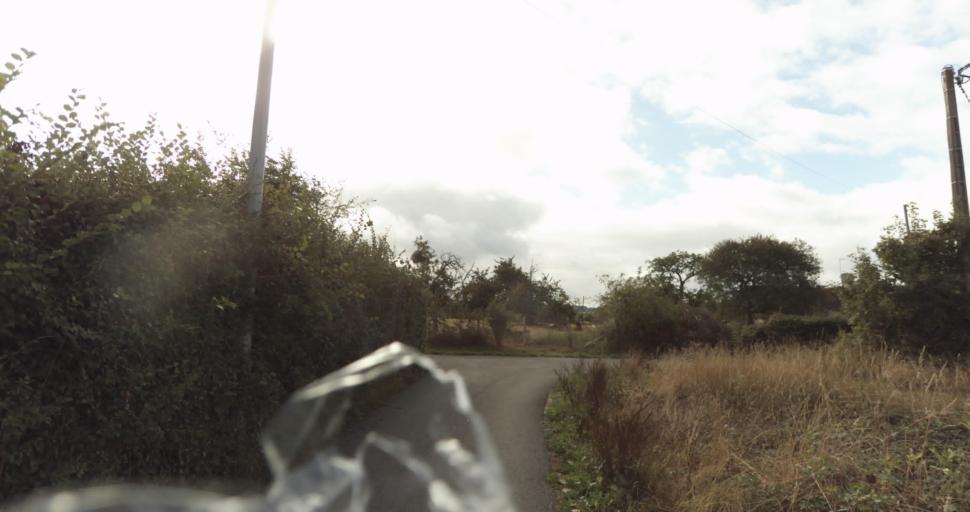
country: FR
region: Lower Normandy
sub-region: Departement de l'Orne
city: Gace
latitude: 48.8493
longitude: 0.2954
